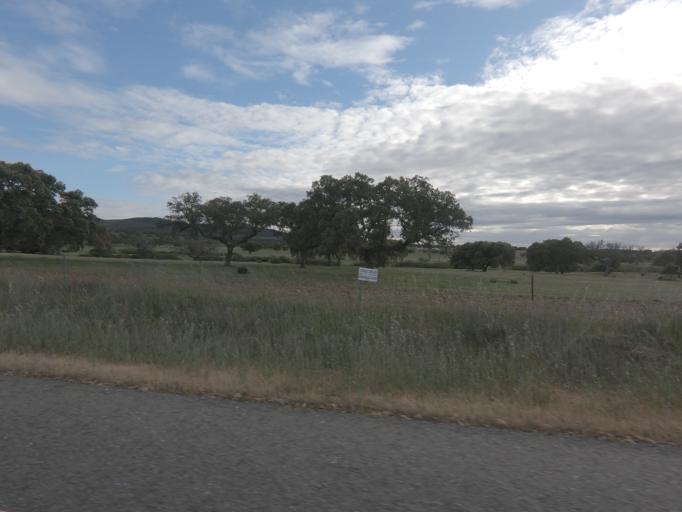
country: ES
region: Extremadura
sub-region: Provincia de Caceres
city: Pedroso de Acim
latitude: 39.8547
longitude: -6.4219
